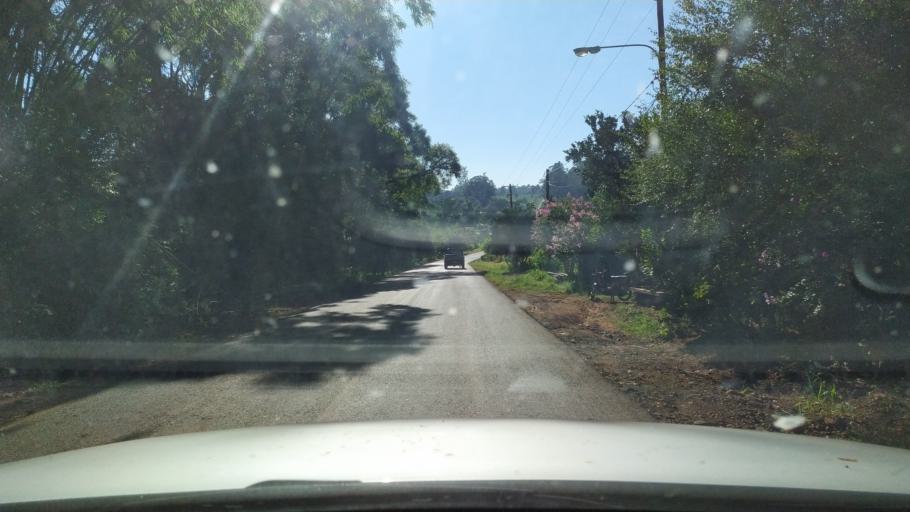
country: AR
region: Misiones
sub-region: Departamento de Montecarlo
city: Montecarlo
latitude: -26.5905
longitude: -54.7173
